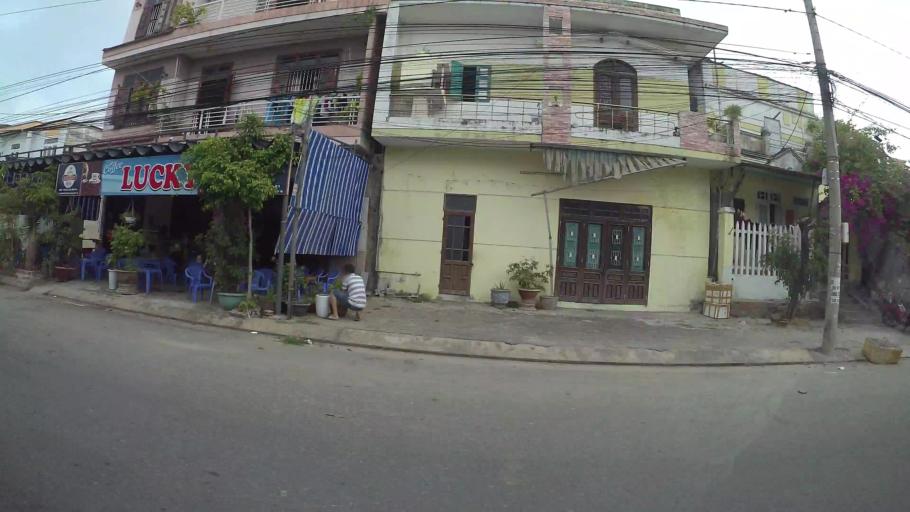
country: VN
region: Da Nang
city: Son Tra
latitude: 16.0830
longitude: 108.2466
